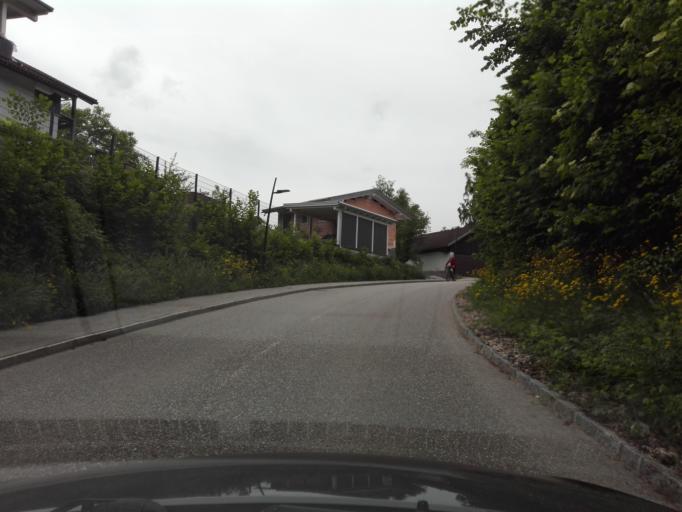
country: AT
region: Upper Austria
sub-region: Politischer Bezirk Gmunden
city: Scharnstein
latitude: 47.9158
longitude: 13.9692
